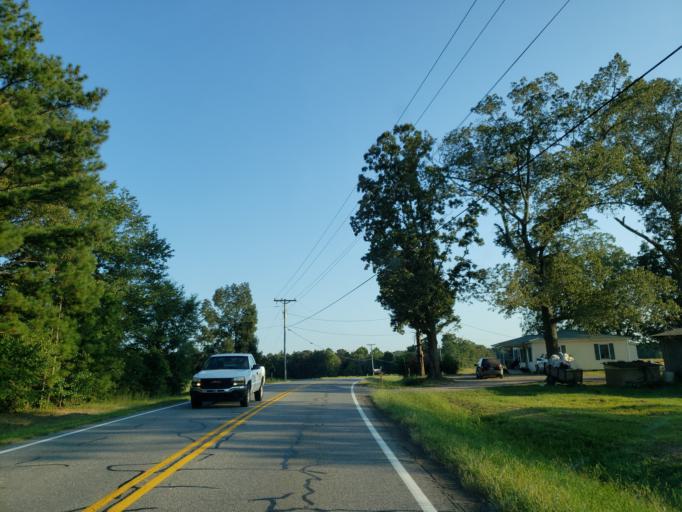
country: US
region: Georgia
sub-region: Gordon County
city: Calhoun
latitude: 34.5575
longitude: -84.8932
